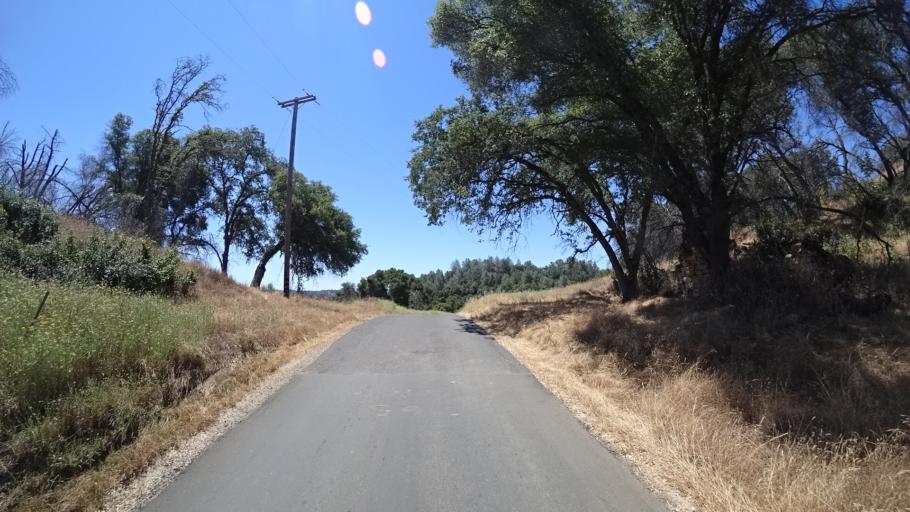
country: US
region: California
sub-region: Calaveras County
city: Mountain Ranch
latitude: 38.1708
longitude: -120.5921
